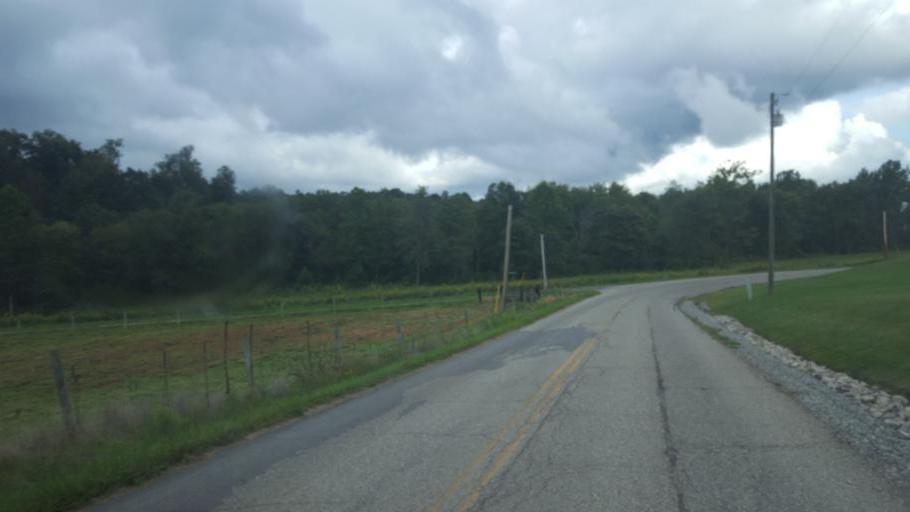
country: US
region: Ohio
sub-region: Jackson County
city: Oak Hill
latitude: 38.9387
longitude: -82.5788
